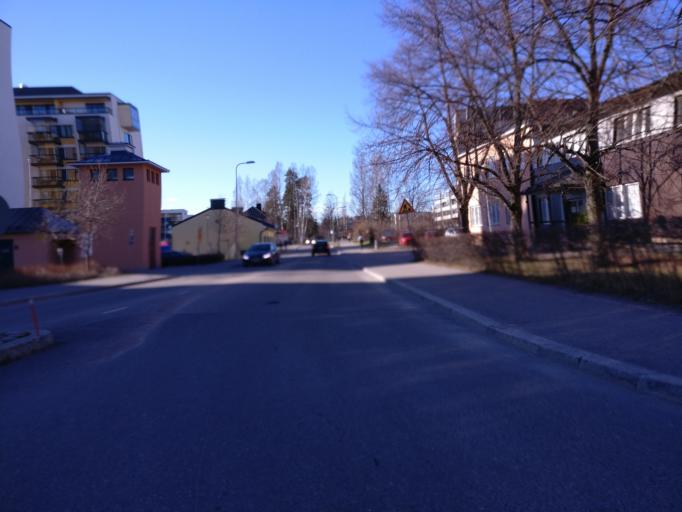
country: FI
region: Uusimaa
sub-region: Helsinki
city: Jaervenpaeae
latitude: 60.4769
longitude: 25.0927
